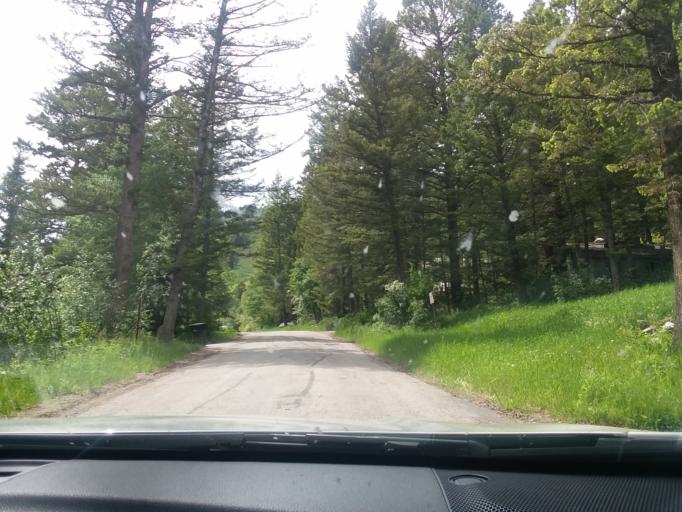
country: US
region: Wyoming
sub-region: Teton County
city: Moose Wilson Road
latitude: 43.5883
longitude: -110.8358
